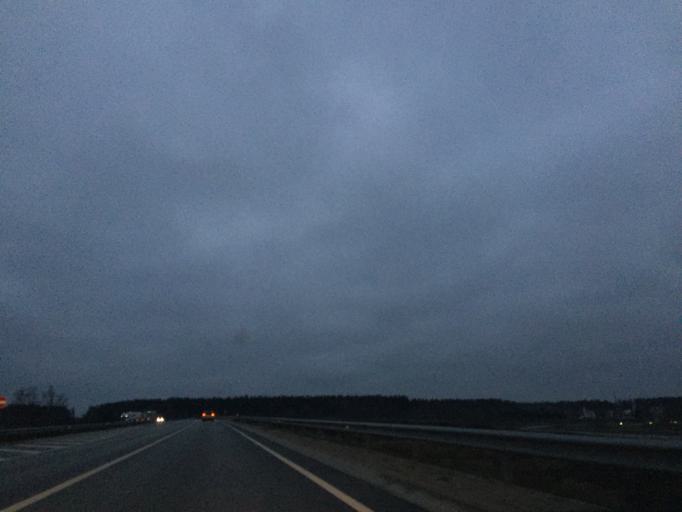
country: LV
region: Koceni
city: Koceni
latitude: 57.5261
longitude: 25.3710
